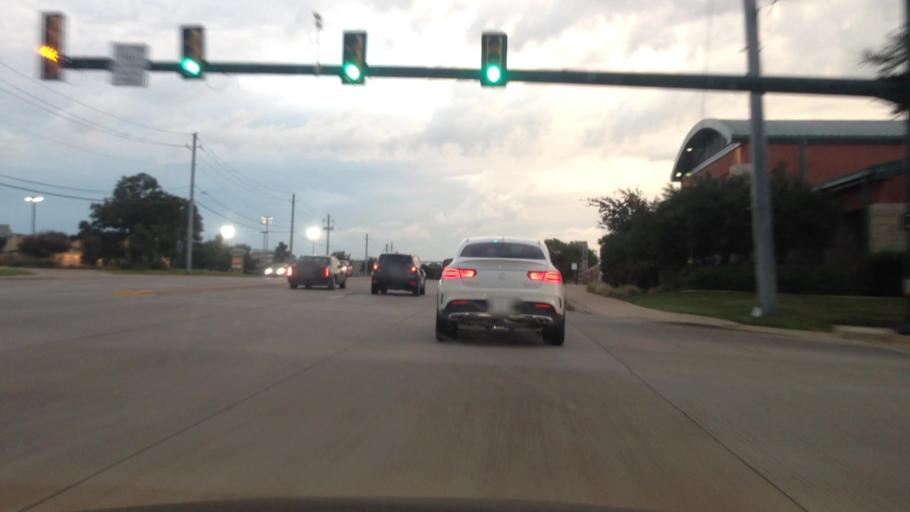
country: US
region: Texas
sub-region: Tarrant County
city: Hurst
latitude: 32.8528
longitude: -97.1860
